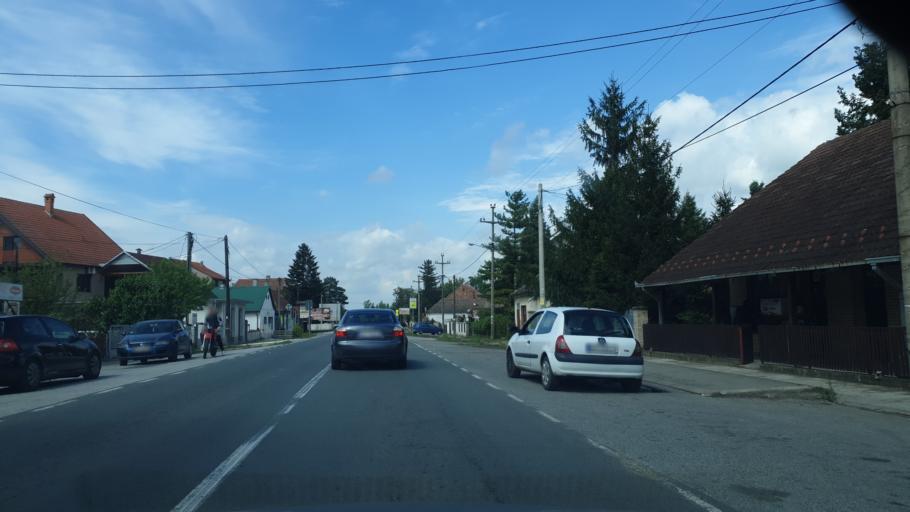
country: RS
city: Stubline
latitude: 44.5725
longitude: 20.1513
